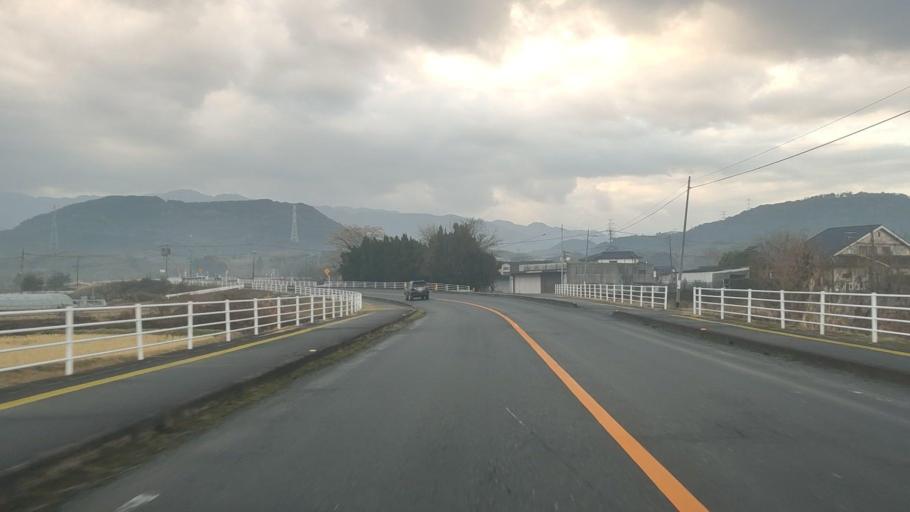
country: JP
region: Kumamoto
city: Matsubase
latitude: 32.6456
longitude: 130.8117
